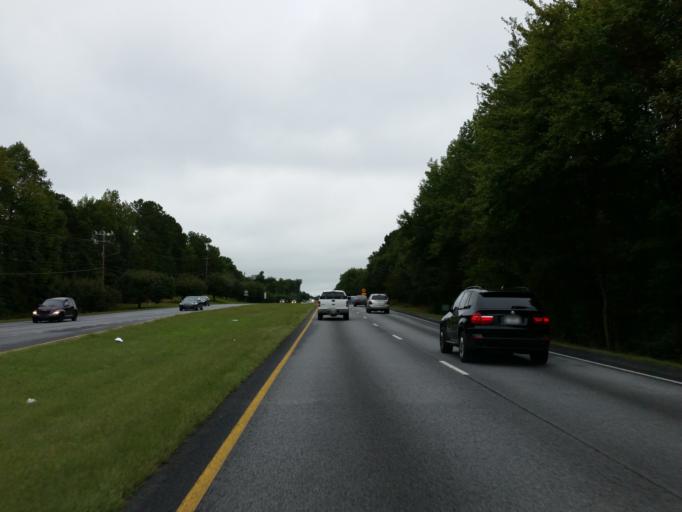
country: US
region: Georgia
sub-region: Clayton County
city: Jonesboro
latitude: 33.5044
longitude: -84.3521
